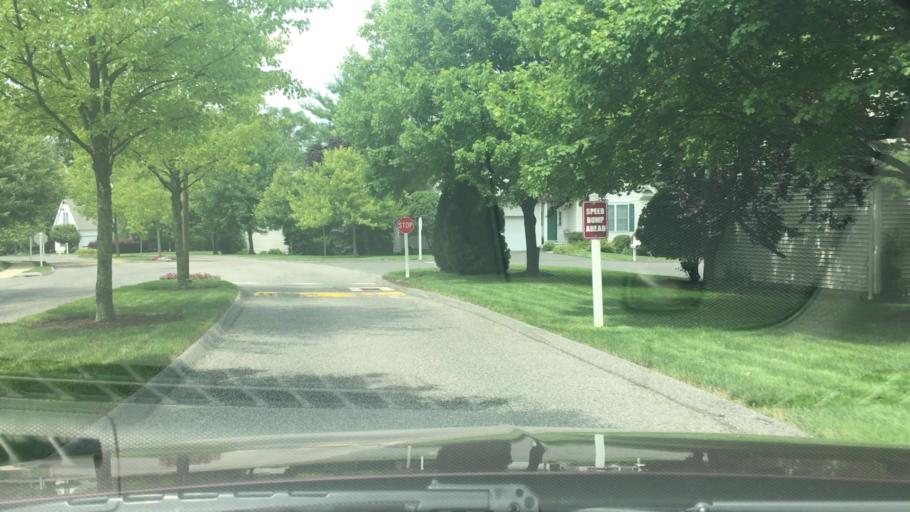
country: US
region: Connecticut
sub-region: Fairfield County
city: Danbury
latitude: 41.4324
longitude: -73.4205
